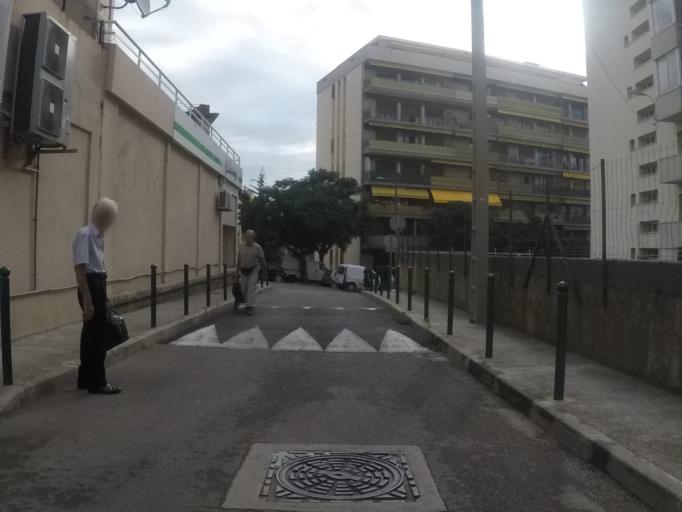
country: FR
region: Corsica
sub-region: Departement de la Corse-du-Sud
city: Ajaccio
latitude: 41.9136
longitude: 8.7249
